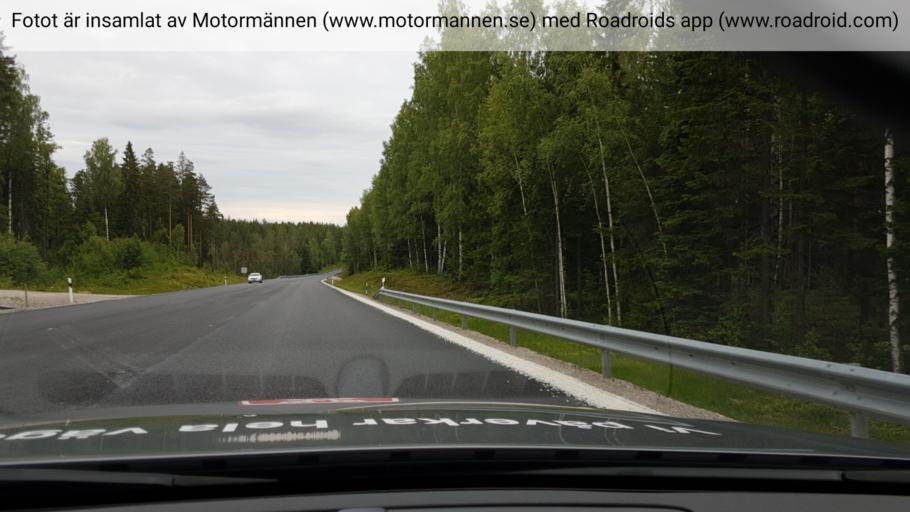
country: SE
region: Vaestmanland
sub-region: Skinnskattebergs Kommun
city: Skinnskatteberg
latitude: 59.8531
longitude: 15.5866
